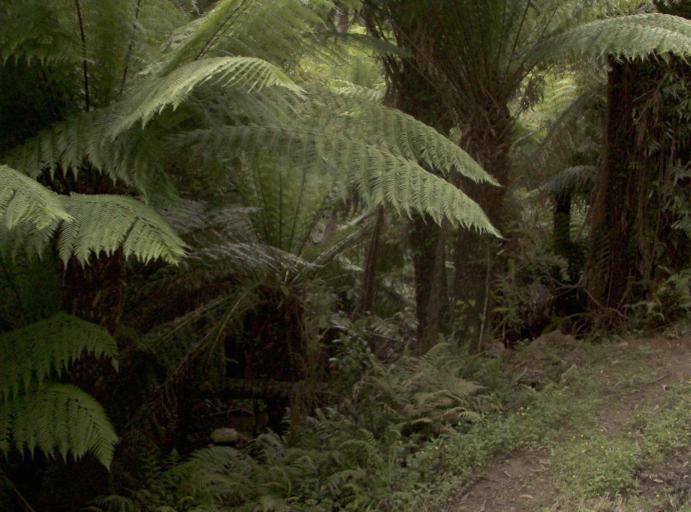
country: AU
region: Victoria
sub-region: Latrobe
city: Traralgon
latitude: -38.4537
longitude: 146.5408
